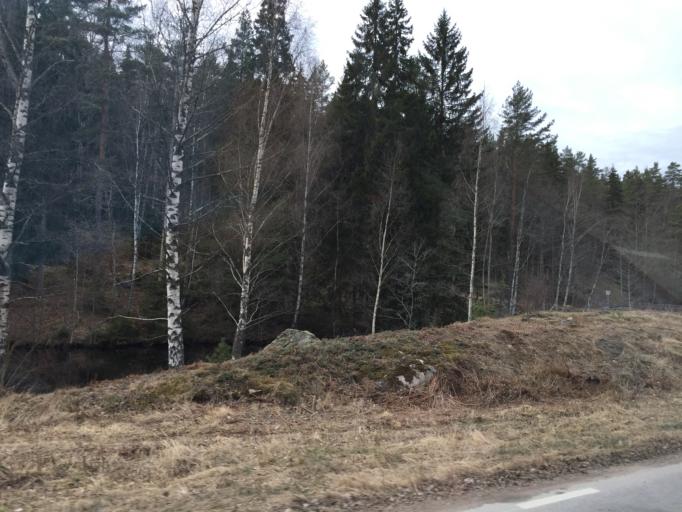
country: SE
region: OEstergoetland
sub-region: Finspangs Kommun
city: Finspang
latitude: 58.7491
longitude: 15.8285
